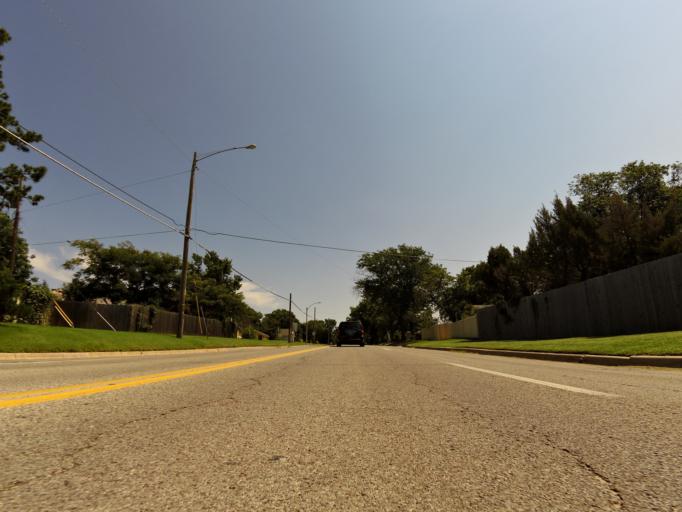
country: US
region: Kansas
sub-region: Sedgwick County
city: Wichita
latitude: 37.6865
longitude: -97.2683
